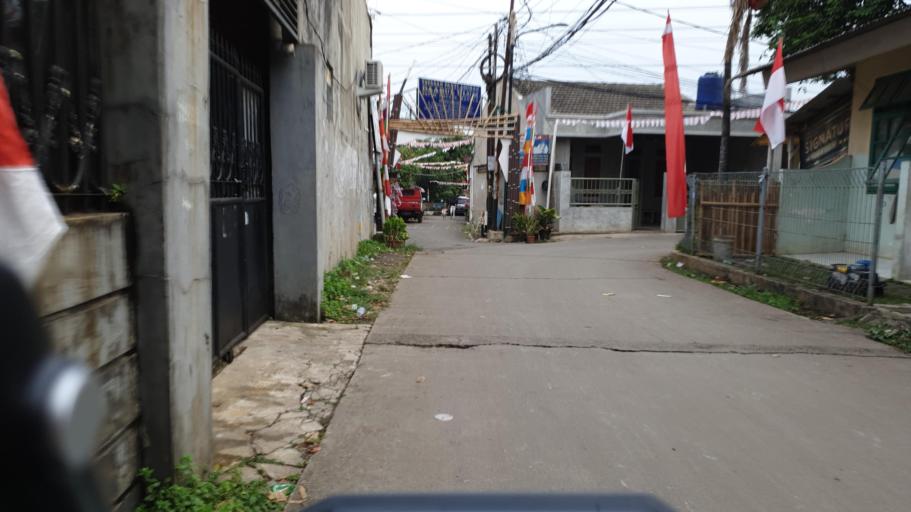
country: ID
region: West Java
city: Pamulang
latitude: -6.3226
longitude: 106.7699
